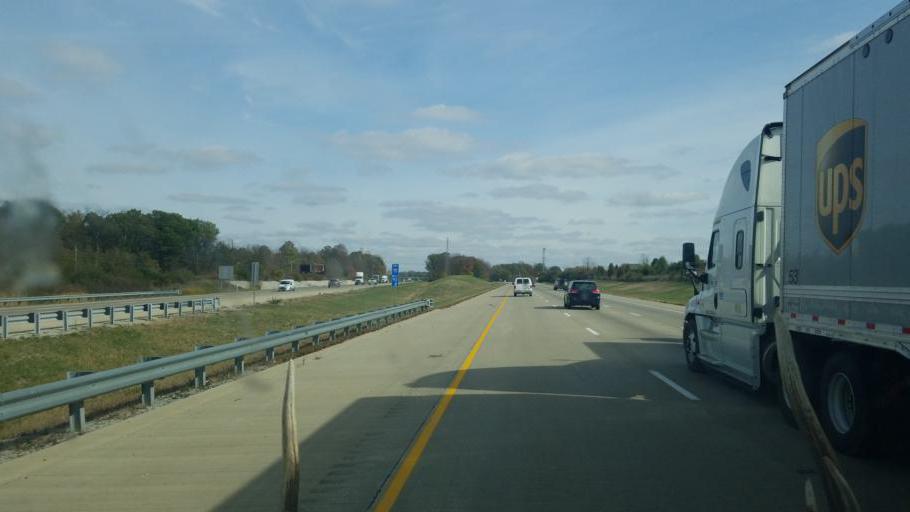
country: US
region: Indiana
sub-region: Marion County
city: Cumberland
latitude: 39.8032
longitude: -85.9710
